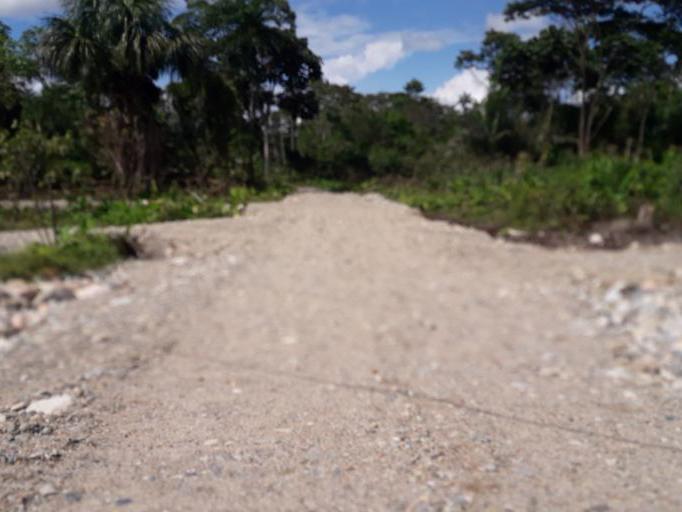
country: EC
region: Napo
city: Tena
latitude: -0.9562
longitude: -77.8207
